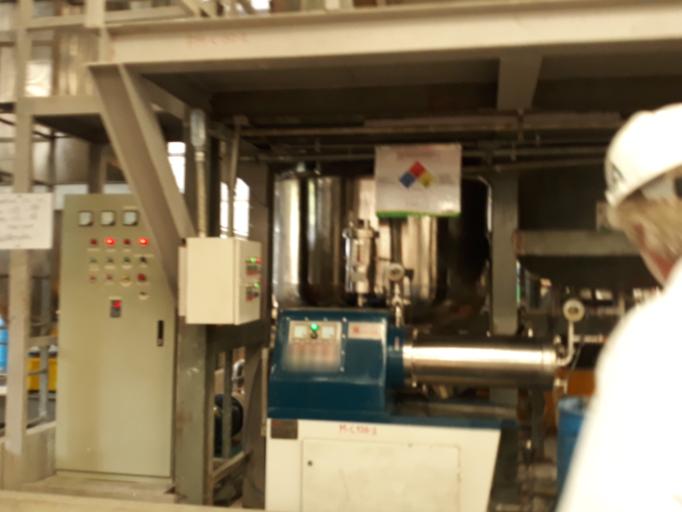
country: GT
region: Escuintla
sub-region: Municipio de Masagua
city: Masagua
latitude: 14.2147
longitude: -90.7569
